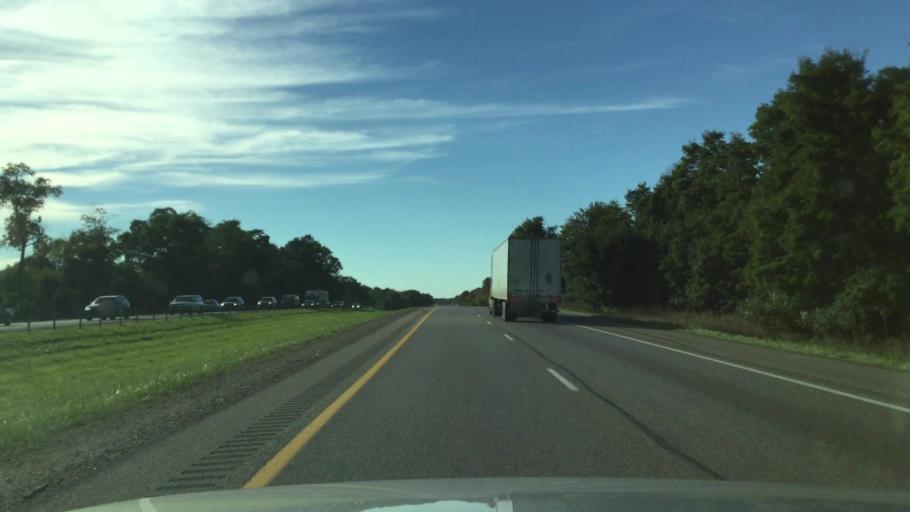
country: US
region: Michigan
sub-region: Calhoun County
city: Springfield
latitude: 42.2775
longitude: -85.3213
